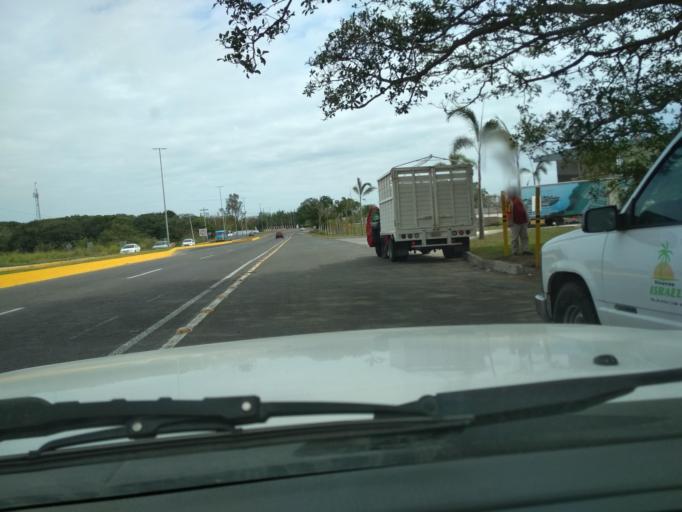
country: MX
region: Veracruz
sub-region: Alvarado
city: Playa de la Libertad
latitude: 19.0869
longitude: -96.1184
